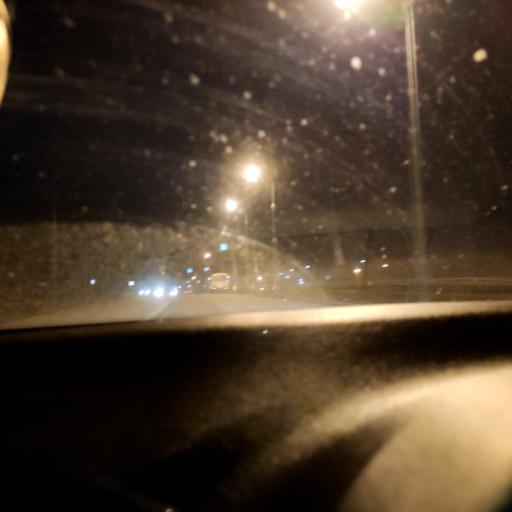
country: RU
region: Samara
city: Petra-Dubrava
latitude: 53.3044
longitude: 50.3128
